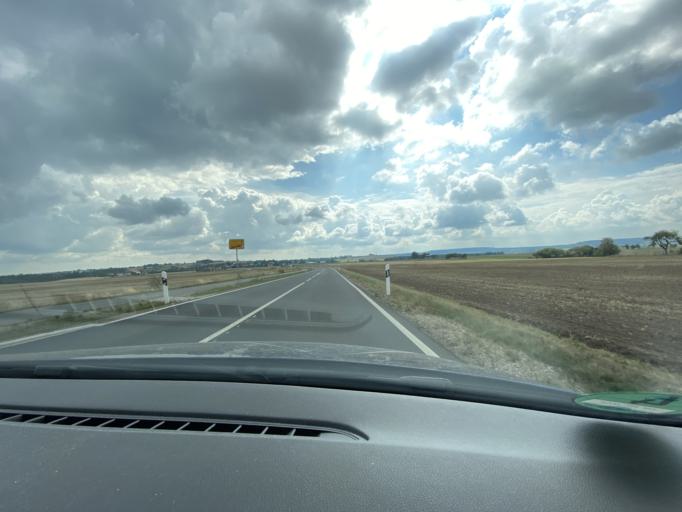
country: DE
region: Saxony
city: Tharandt
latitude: 51.0161
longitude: 13.5866
